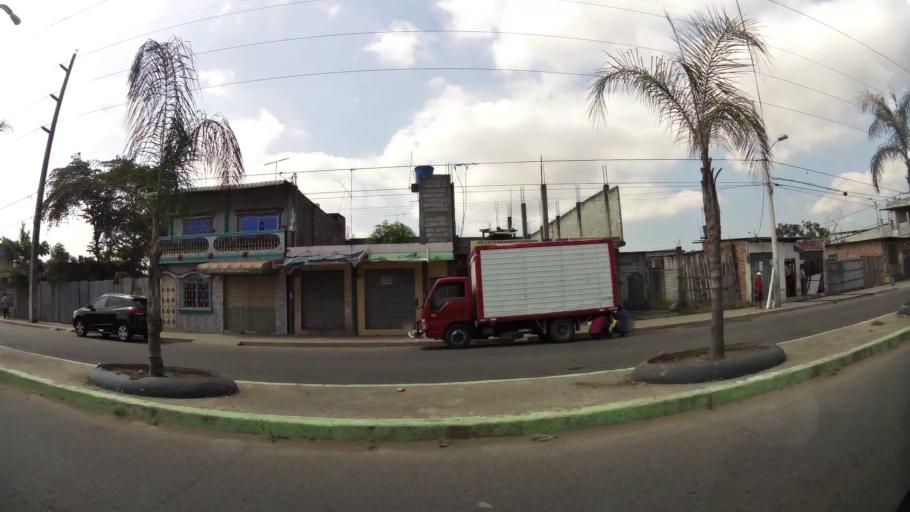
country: EC
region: Guayas
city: Eloy Alfaro
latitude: -2.1627
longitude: -79.8341
